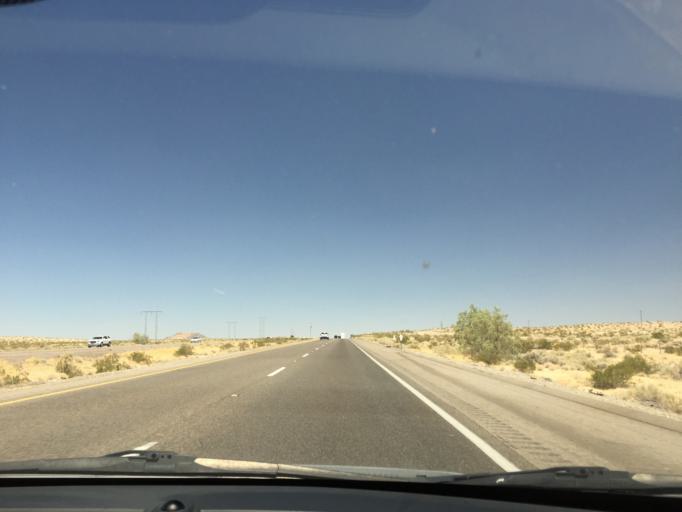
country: US
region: California
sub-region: San Bernardino County
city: Fort Irwin
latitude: 35.0072
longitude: -116.5413
